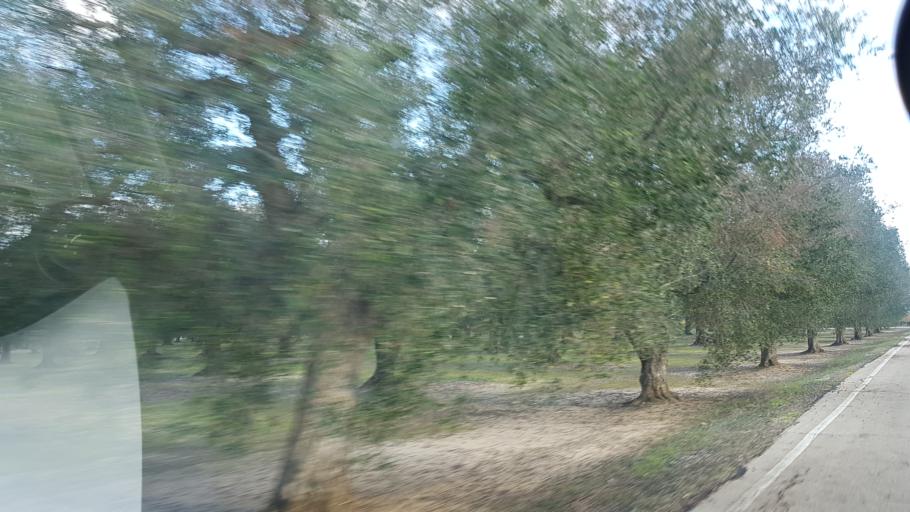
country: IT
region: Apulia
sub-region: Provincia di Brindisi
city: San Pietro Vernotico
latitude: 40.5124
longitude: 18.0166
